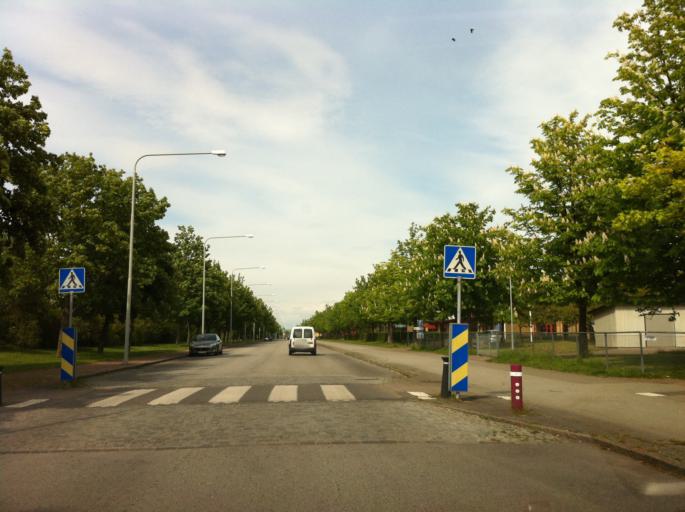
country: SE
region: Skane
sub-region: Landskrona
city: Landskrona
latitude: 55.8891
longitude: 12.8415
